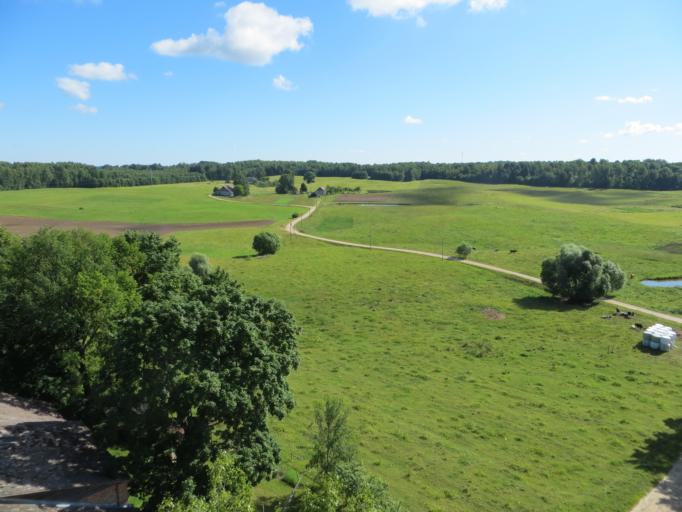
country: LT
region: Utenos apskritis
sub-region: Utena
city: Utena
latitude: 55.5476
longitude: 25.7196
